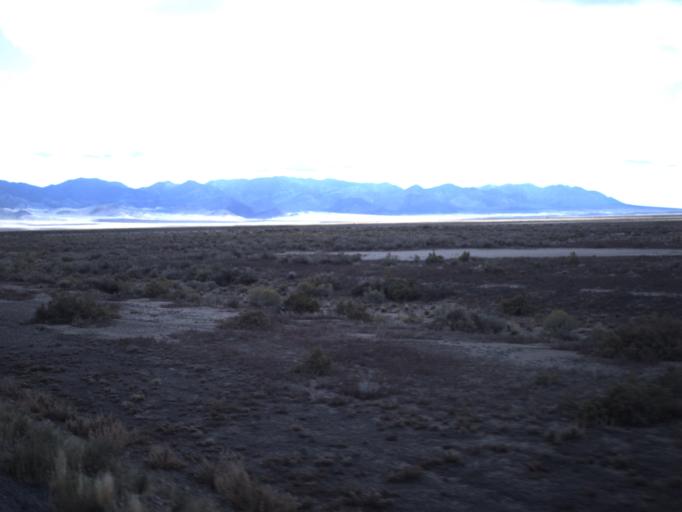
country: US
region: Utah
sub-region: Beaver County
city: Milford
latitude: 38.5434
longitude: -113.7119
